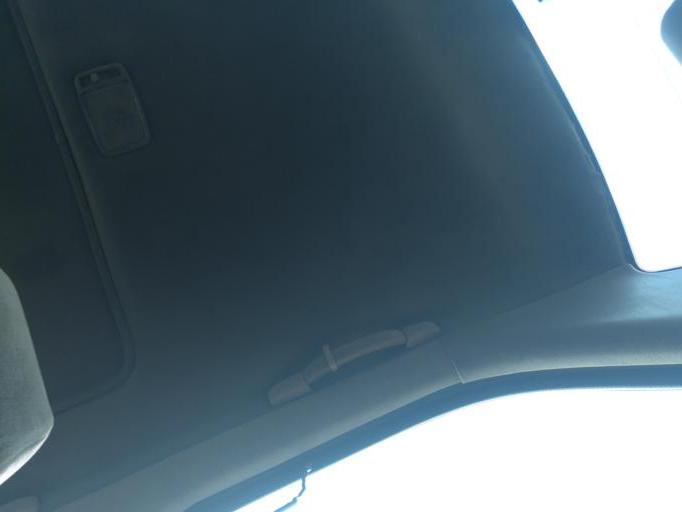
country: NG
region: Lagos
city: Ikorodu
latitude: 6.6411
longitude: 3.5498
